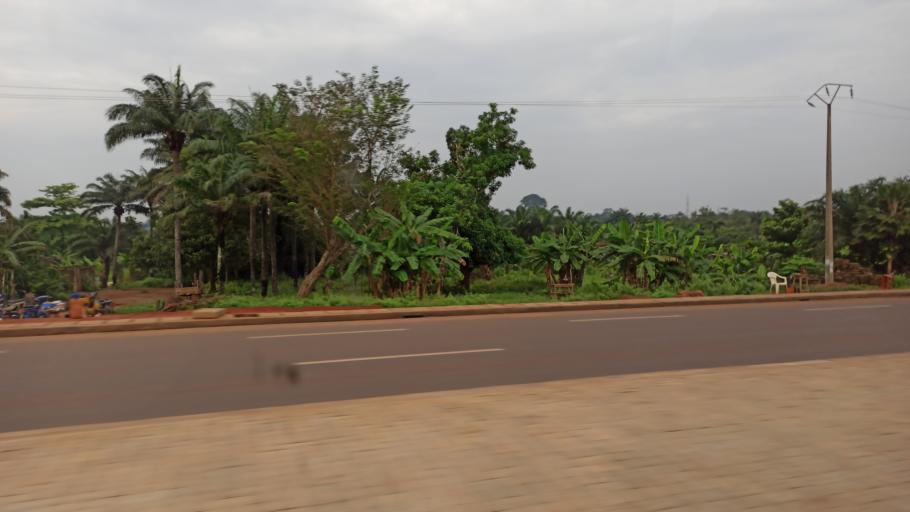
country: BJ
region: Queme
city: Porto-Novo
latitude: 6.5301
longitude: 2.6001
